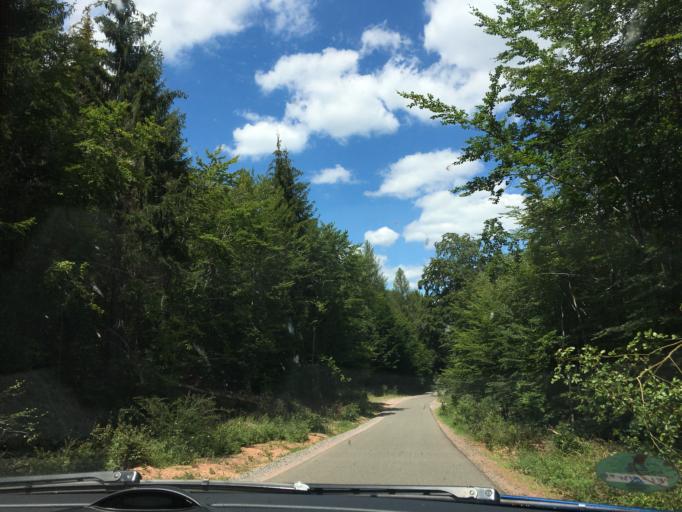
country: DE
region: Rheinland-Pfalz
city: Wilgartswiesen
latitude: 49.2527
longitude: 7.8282
